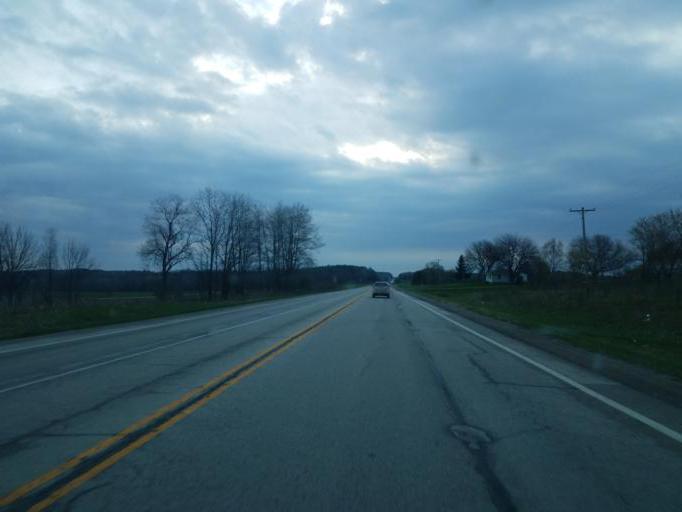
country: US
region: Michigan
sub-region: Isabella County
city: Lake Isabella
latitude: 43.5961
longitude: -85.0101
